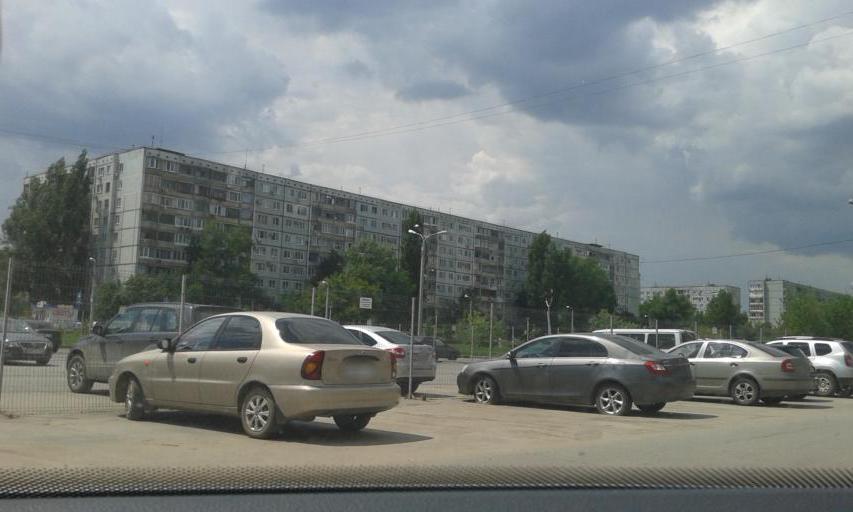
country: RU
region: Volgograd
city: Volgograd
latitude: 48.7518
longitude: 44.5054
